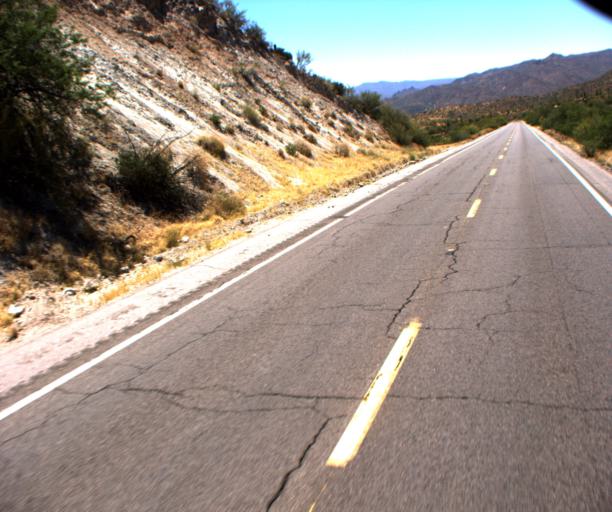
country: US
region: Arizona
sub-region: Pinal County
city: Kearny
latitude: 33.1437
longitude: -110.9915
